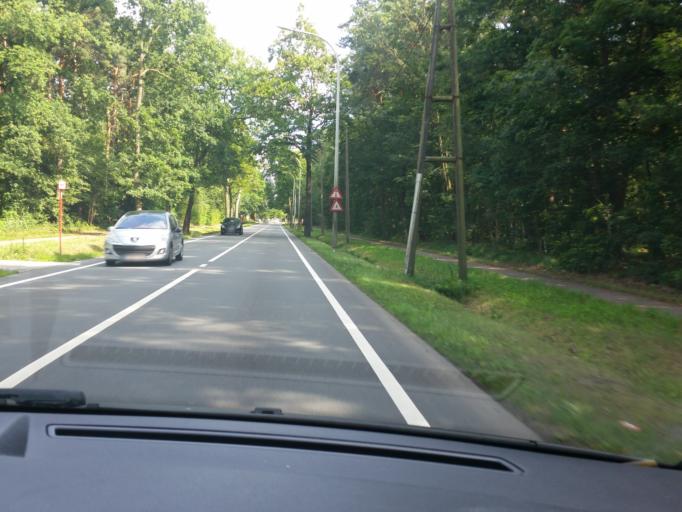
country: BE
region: Flanders
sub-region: Provincie Antwerpen
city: Brasschaat
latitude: 51.3136
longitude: 4.5492
